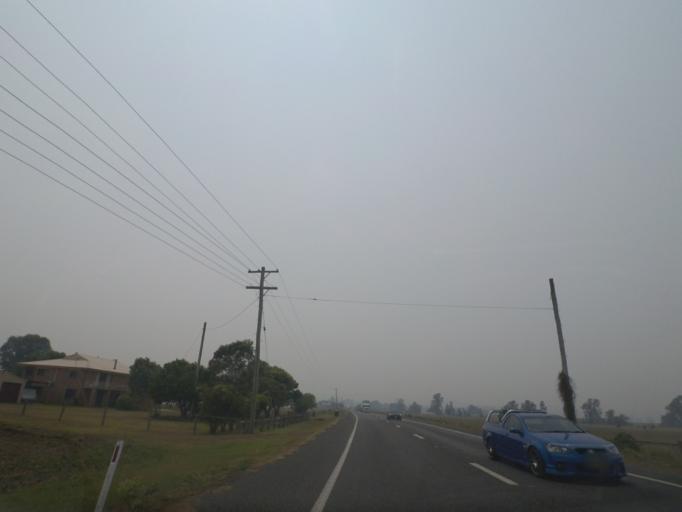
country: AU
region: New South Wales
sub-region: Clarence Valley
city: Maclean
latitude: -29.5652
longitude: 153.1176
